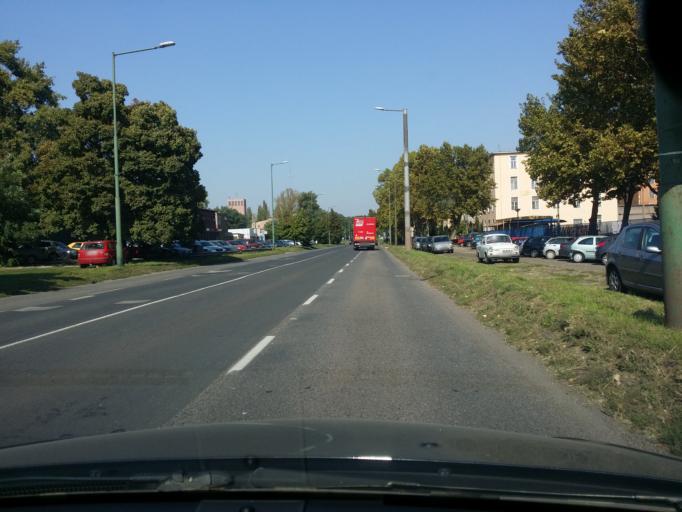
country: HU
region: Fejer
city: Dunaujvaros
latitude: 46.9461
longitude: 18.9509
